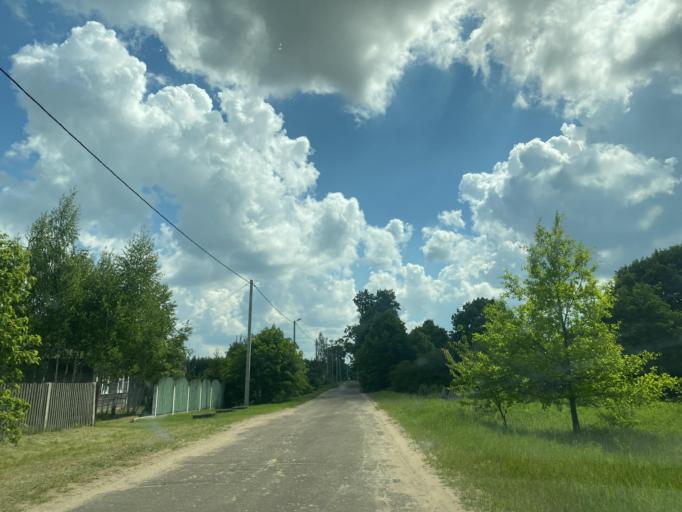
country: BY
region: Brest
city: Ivanava
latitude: 52.2038
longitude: 25.6079
